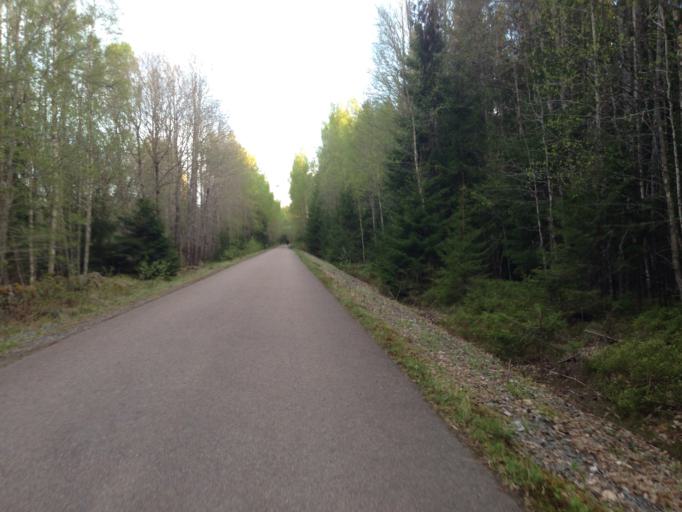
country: SE
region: Dalarna
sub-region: Ludvika Kommun
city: Grangesberg
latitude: 60.1290
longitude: 15.0703
